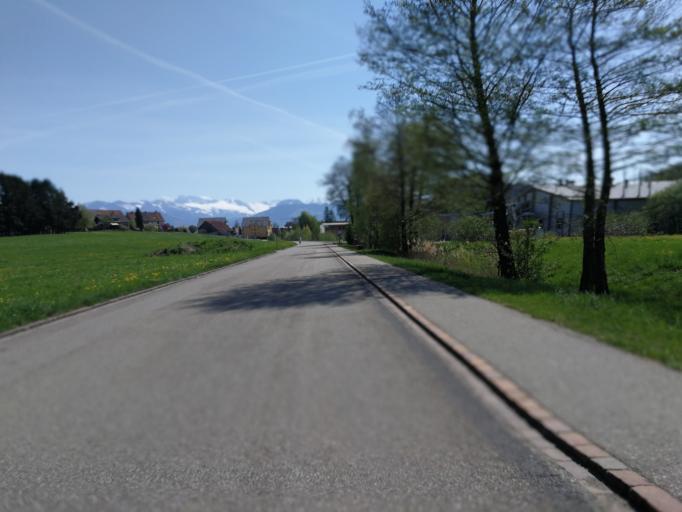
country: CH
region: Zurich
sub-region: Bezirk Hinwil
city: Bubikon
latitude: 47.2788
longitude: 8.8197
